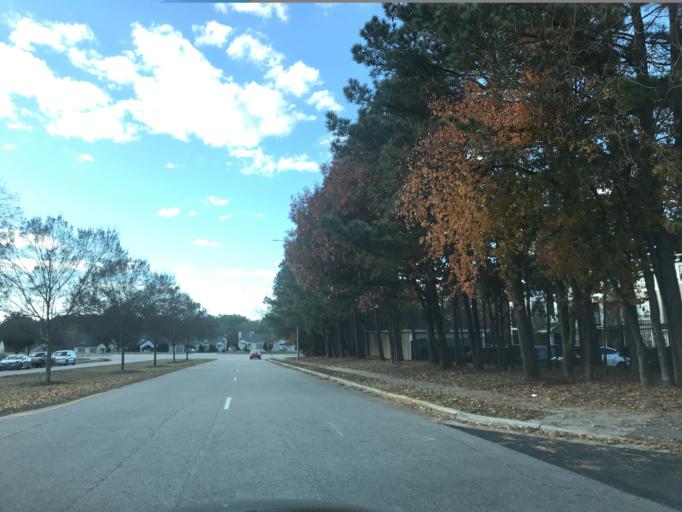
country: US
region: North Carolina
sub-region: Wake County
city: Raleigh
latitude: 35.8461
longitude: -78.5892
